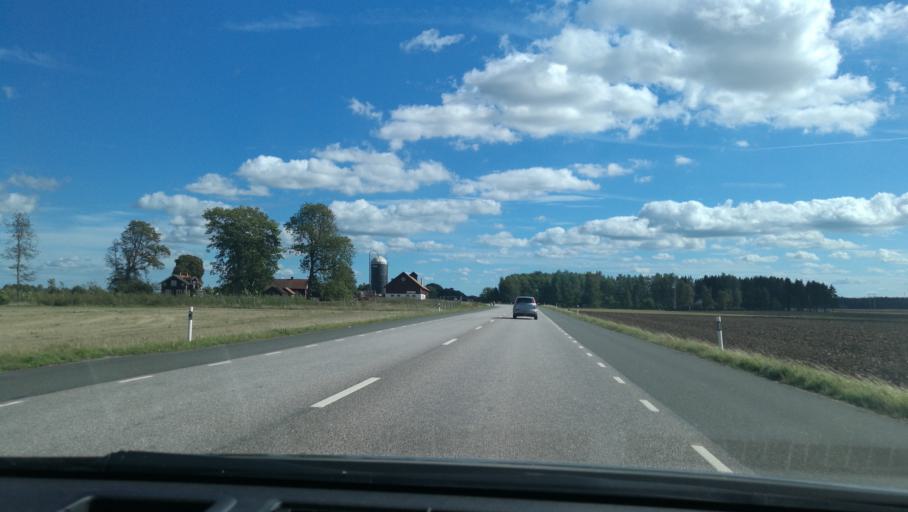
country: SE
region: Vaestra Goetaland
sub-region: Gotene Kommun
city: Kallby
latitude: 58.5090
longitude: 13.3811
